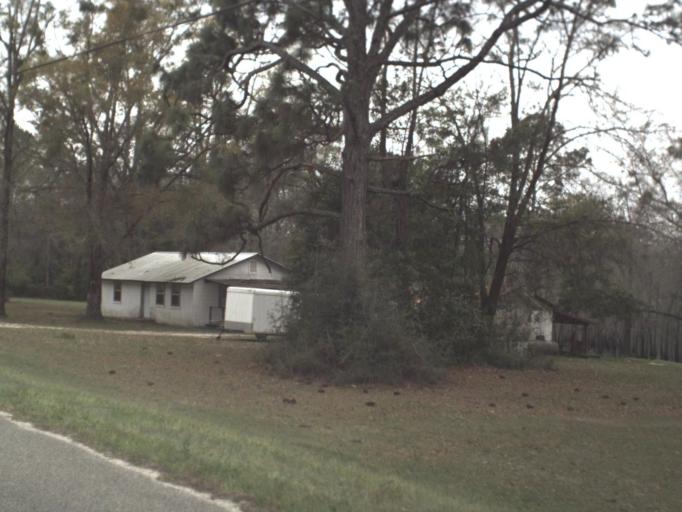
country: US
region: Florida
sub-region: Gulf County
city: Wewahitchka
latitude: 30.1431
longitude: -85.2104
